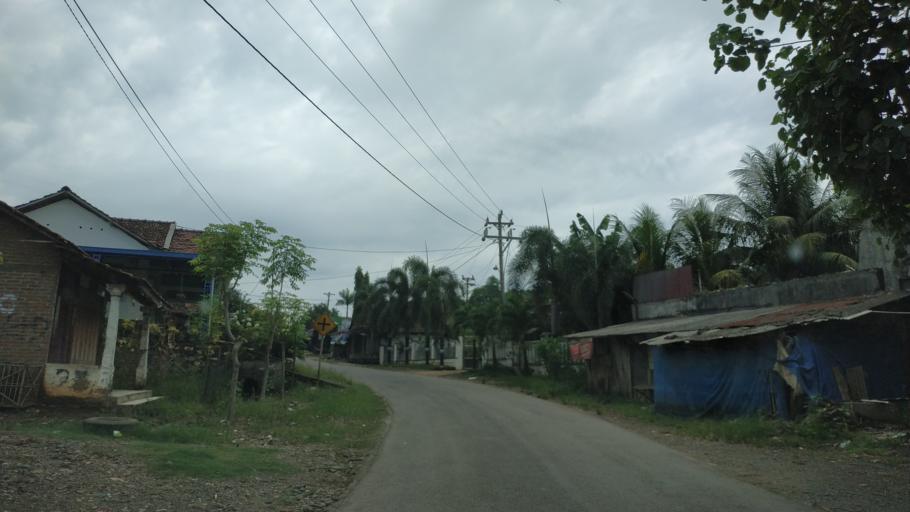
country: ID
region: Central Java
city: Krajan Tegalombo
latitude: -6.4427
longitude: 110.9827
